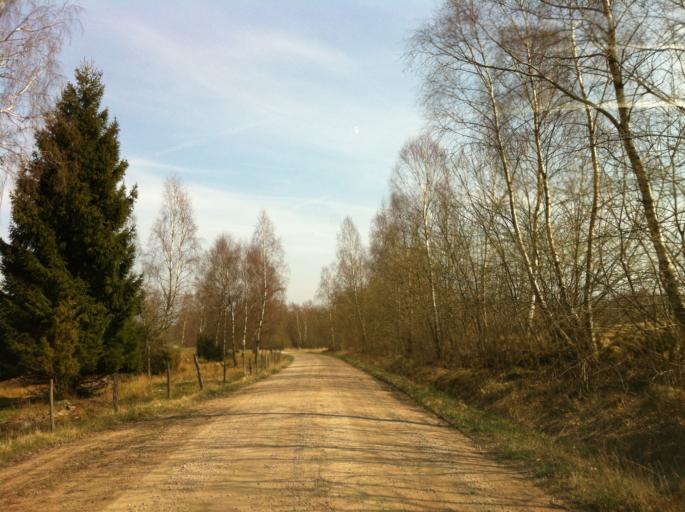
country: SE
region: Skane
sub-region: Eslovs Kommun
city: Stehag
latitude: 56.0073
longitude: 13.3373
